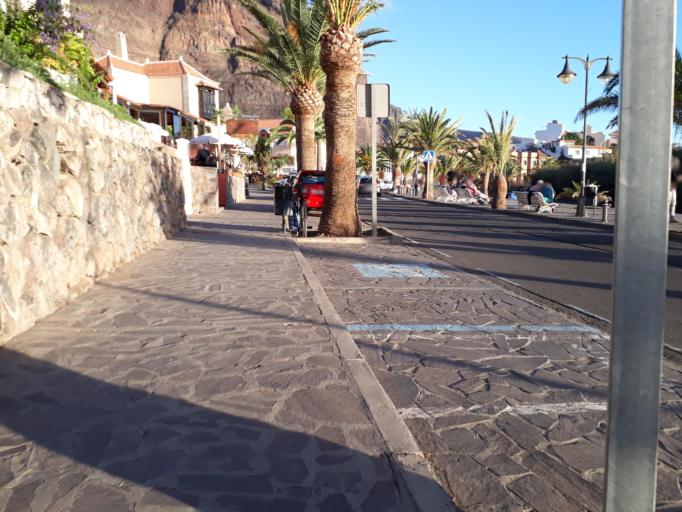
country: ES
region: Canary Islands
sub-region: Provincia de Santa Cruz de Tenerife
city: Alajero
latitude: 28.0861
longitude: -17.3376
